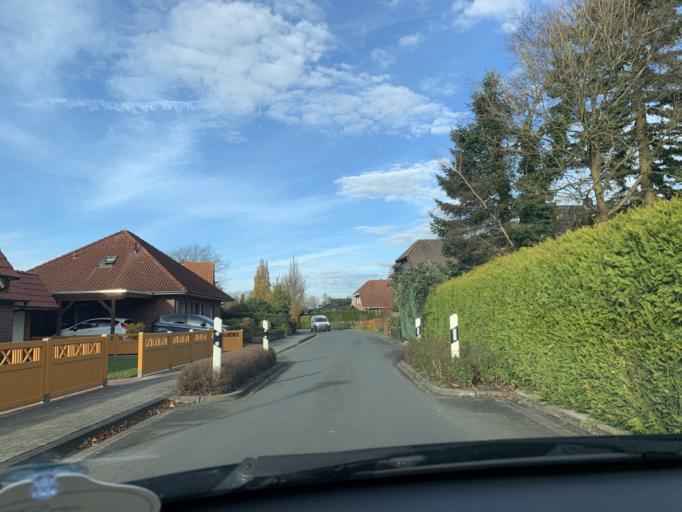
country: DE
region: Lower Saxony
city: Apen
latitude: 53.2202
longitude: 7.8124
